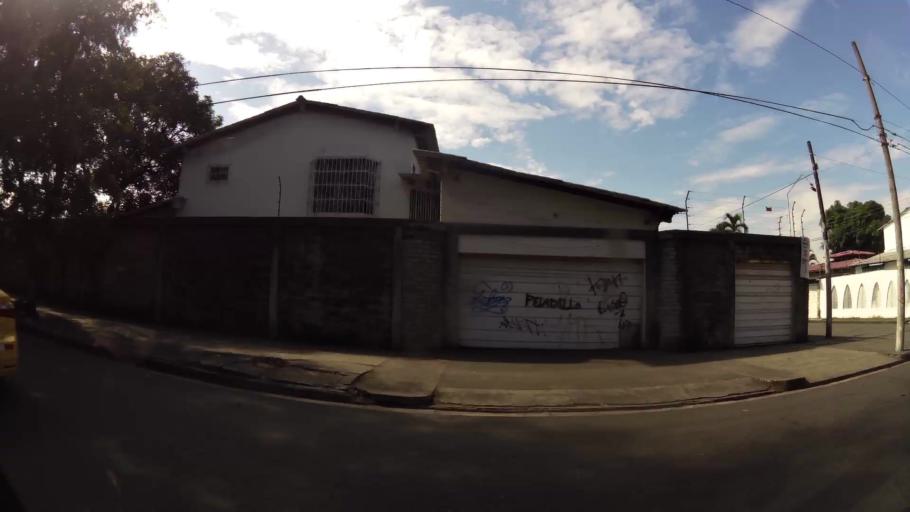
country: EC
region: Guayas
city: Guayaquil
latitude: -2.2232
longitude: -79.8959
